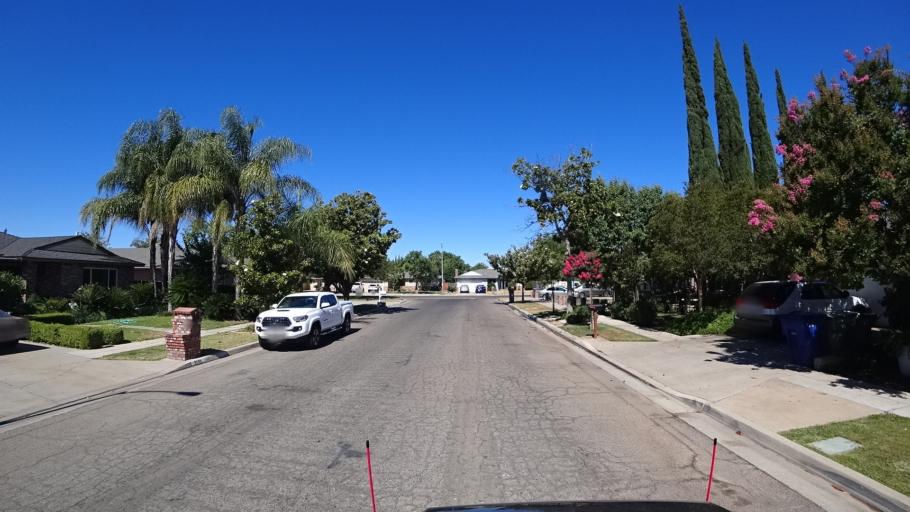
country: US
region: California
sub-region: Fresno County
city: West Park
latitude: 36.7996
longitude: -119.8478
